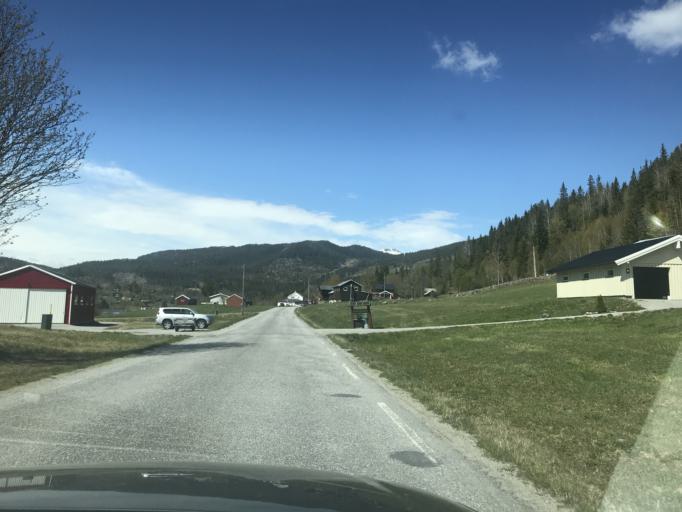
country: NO
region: Telemark
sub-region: Hjartdal
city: Sauland
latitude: 59.7488
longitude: 8.8021
